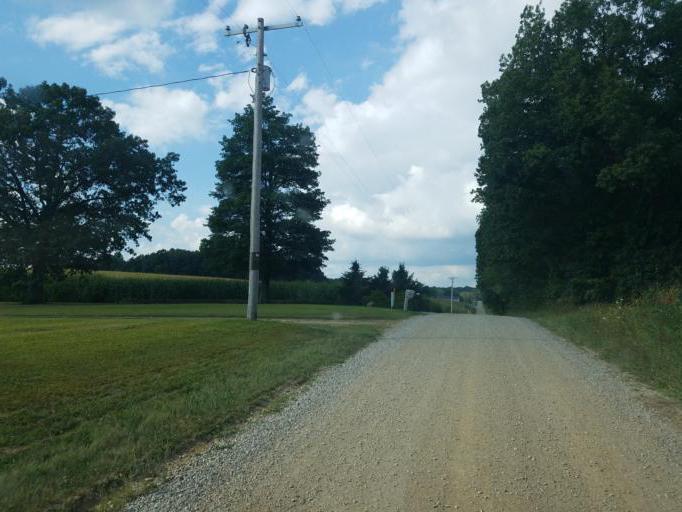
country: US
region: Ohio
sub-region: Knox County
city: Danville
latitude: 40.4968
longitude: -82.3343
